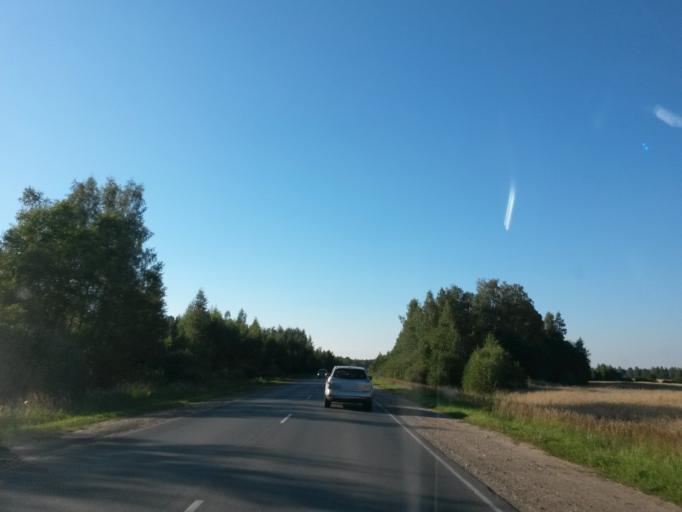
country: RU
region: Ivanovo
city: Novo-Talitsy
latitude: 57.0339
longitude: 40.7488
